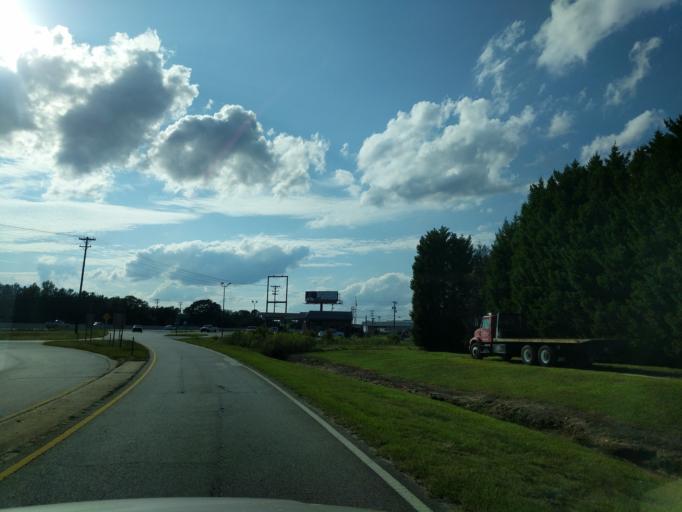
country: US
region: South Carolina
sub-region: Greenville County
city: Fountain Inn
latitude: 34.6897
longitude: -82.2183
